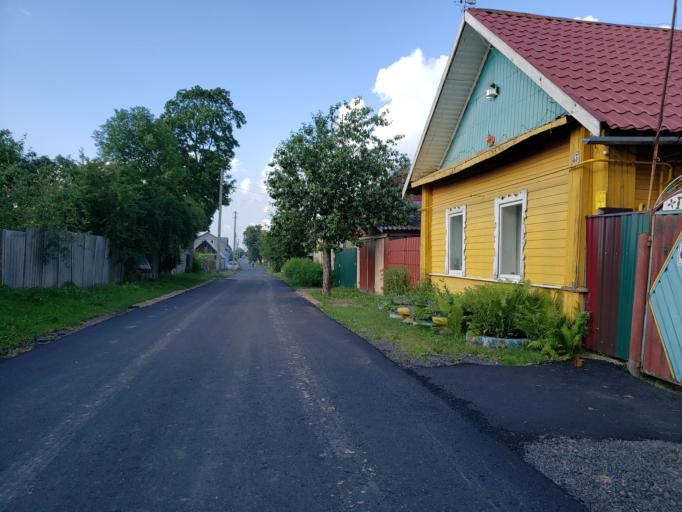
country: BY
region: Minsk
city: Chervyen'
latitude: 53.7068
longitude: 28.4260
